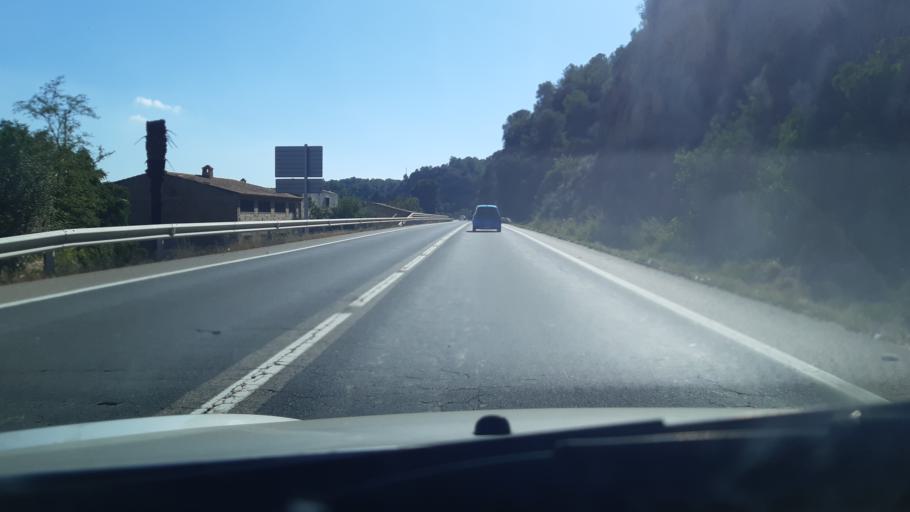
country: ES
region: Catalonia
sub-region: Provincia de Tarragona
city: Tivenys
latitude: 40.8743
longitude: 0.5010
